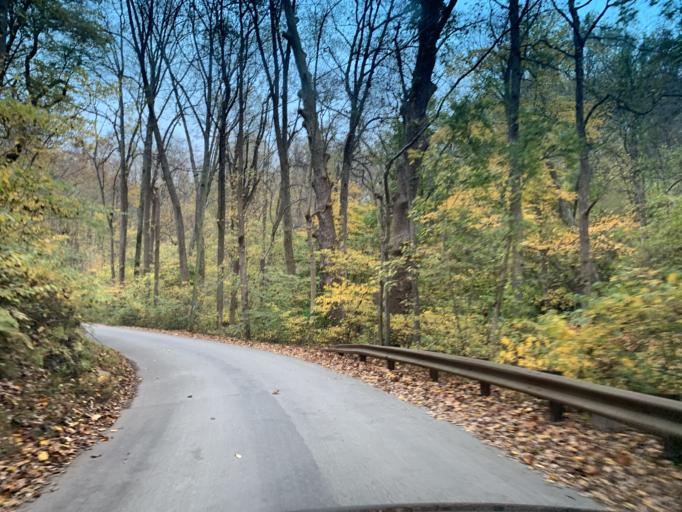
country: US
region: Maryland
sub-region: Harford County
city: Havre de Grace
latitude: 39.6080
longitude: -76.1446
